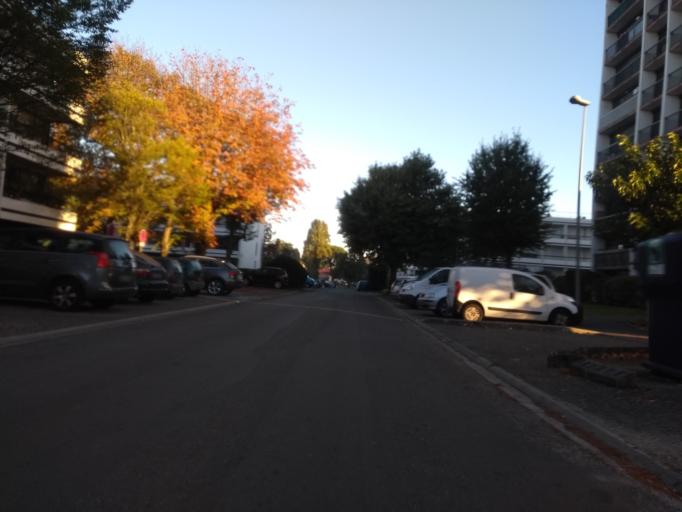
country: FR
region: Aquitaine
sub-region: Departement de la Gironde
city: Pessac
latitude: 44.7914
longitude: -0.6313
